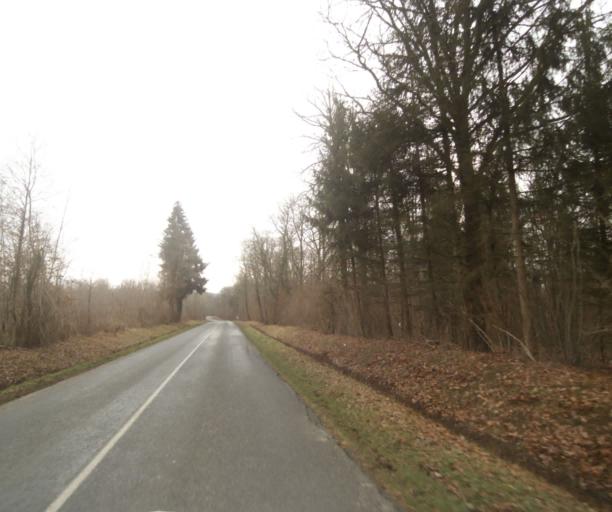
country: FR
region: Champagne-Ardenne
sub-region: Departement de la Marne
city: Pargny-sur-Saulx
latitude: 48.7343
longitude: 4.8620
